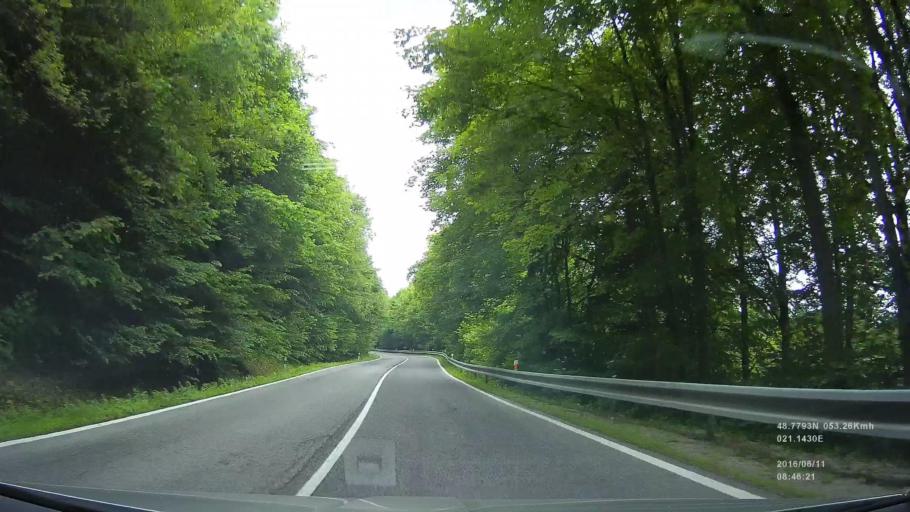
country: SK
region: Kosicky
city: Kosice
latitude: 48.7755
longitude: 21.1481
